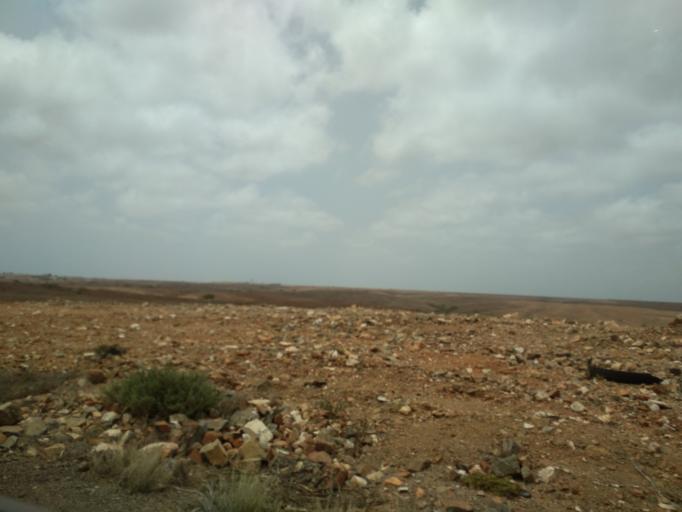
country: CV
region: Sal
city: Espargos
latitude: 16.7596
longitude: -22.9629
